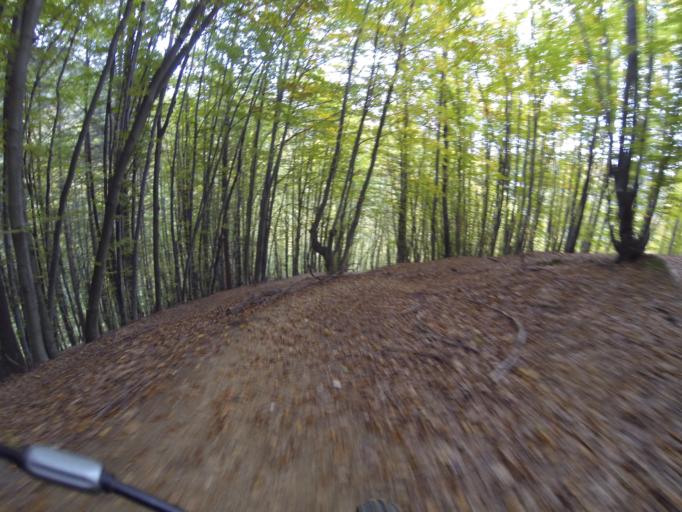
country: RO
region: Gorj
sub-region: Comuna Tismana
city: Sohodol
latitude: 45.0821
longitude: 22.8858
